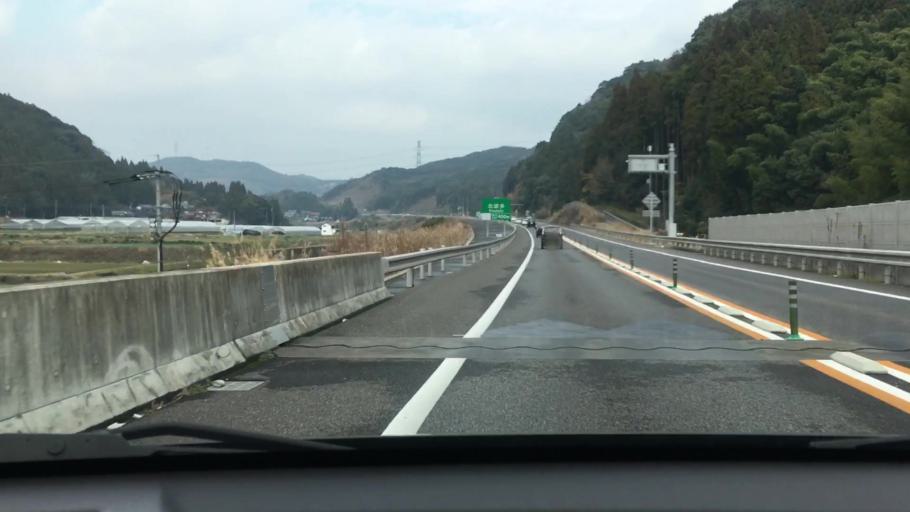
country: JP
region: Saga Prefecture
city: Karatsu
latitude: 33.3771
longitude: 129.9325
